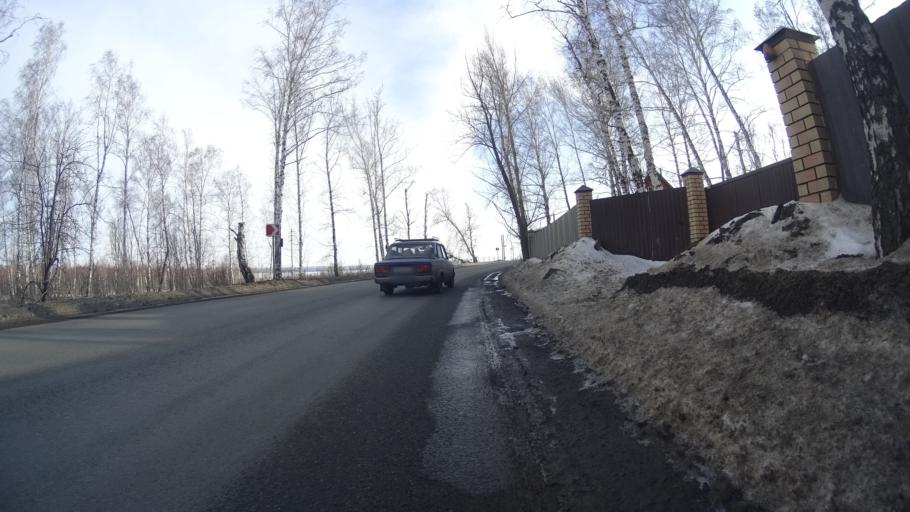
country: RU
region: Chelyabinsk
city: Sargazy
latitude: 55.1255
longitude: 61.2896
